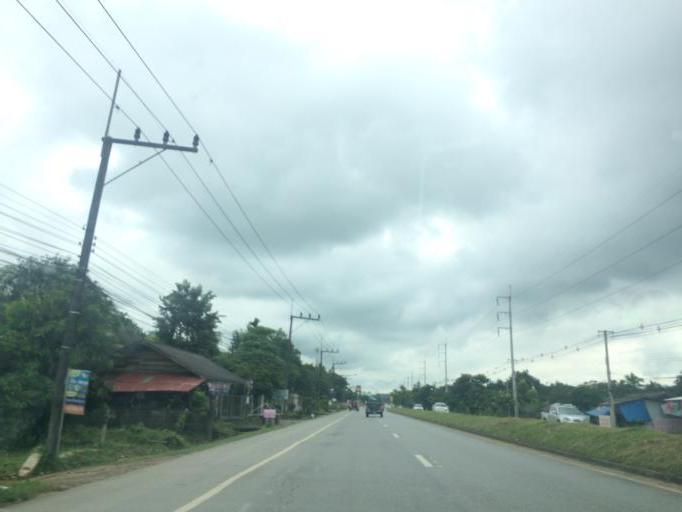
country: TH
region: Chiang Rai
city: Mae Chan
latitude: 20.0780
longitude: 99.8753
